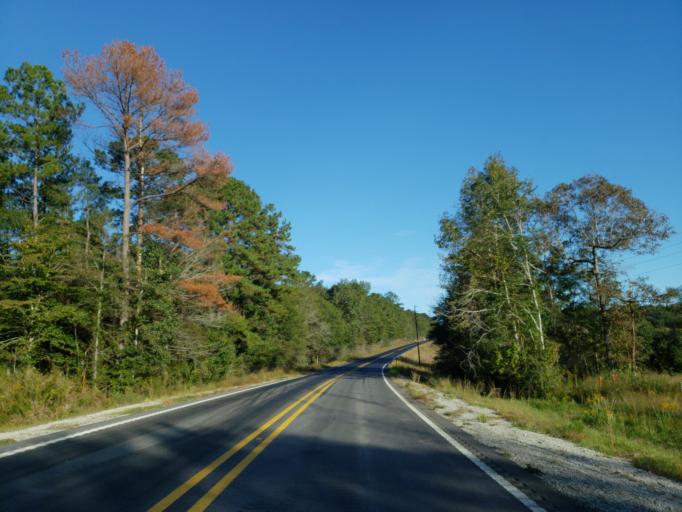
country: US
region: Mississippi
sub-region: Perry County
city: Richton
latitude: 31.3744
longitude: -88.8323
